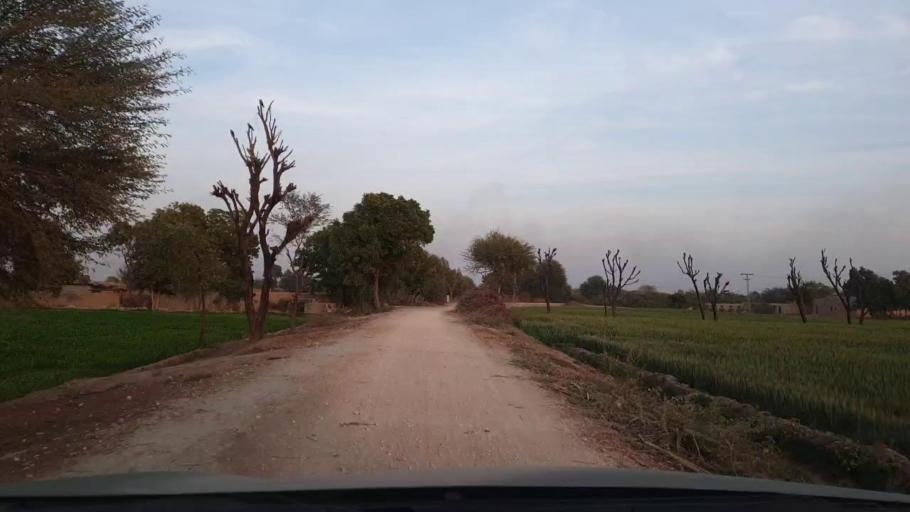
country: PK
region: Sindh
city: Tando Adam
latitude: 25.6676
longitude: 68.7118
